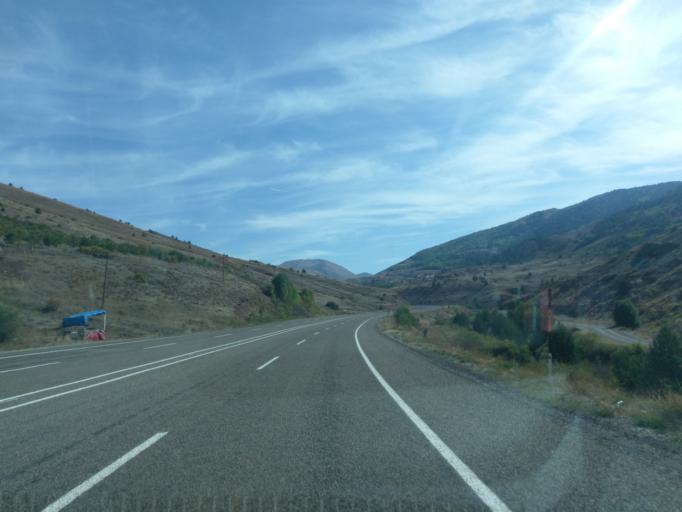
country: TR
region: Sivas
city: Imranli
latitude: 39.8549
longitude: 38.3017
